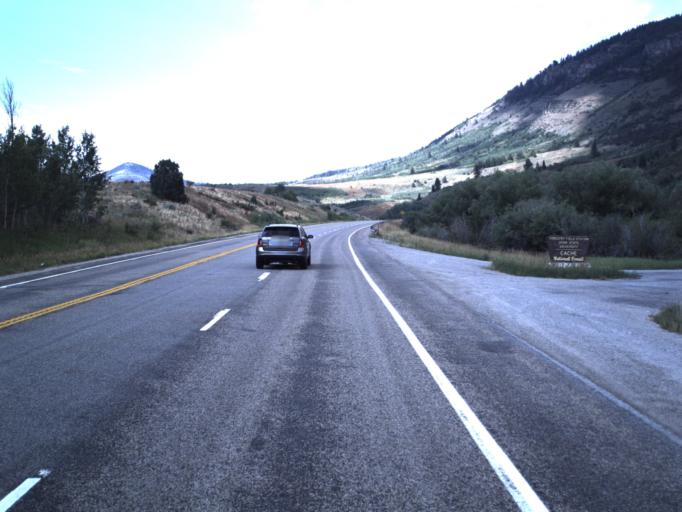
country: US
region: Utah
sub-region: Cache County
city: Richmond
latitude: 41.8756
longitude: -111.5653
